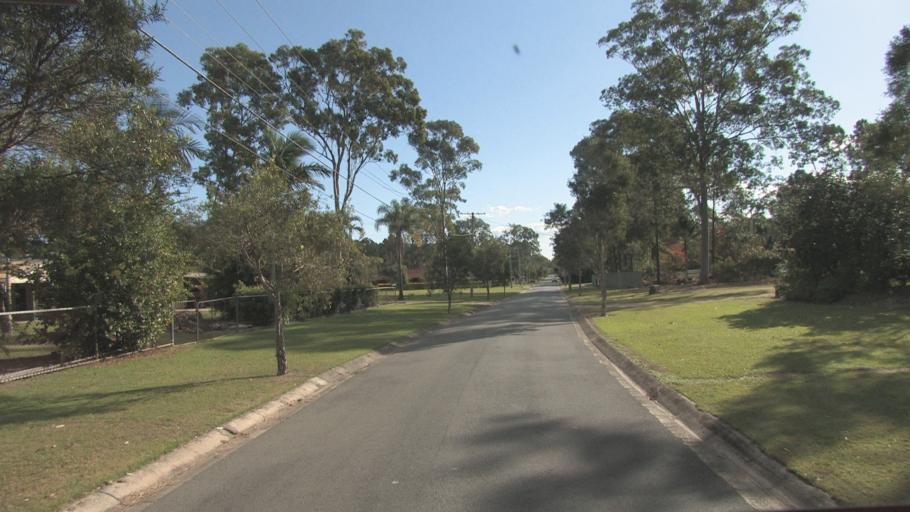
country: AU
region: Queensland
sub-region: Logan
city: Beenleigh
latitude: -27.6717
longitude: 153.2128
